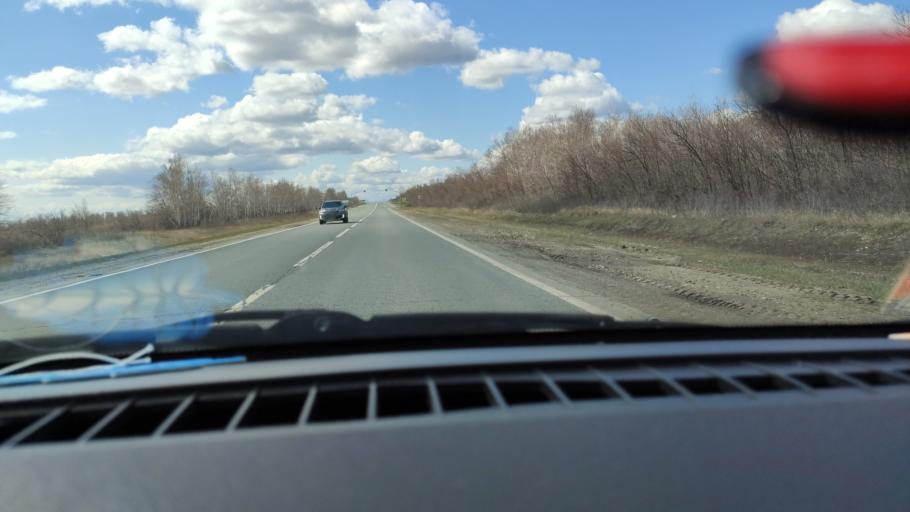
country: RU
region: Saratov
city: Dukhovnitskoye
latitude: 52.6802
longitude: 48.2319
